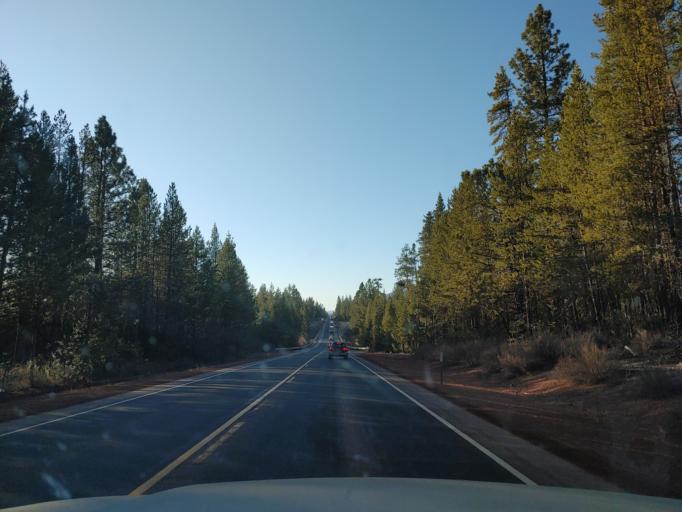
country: US
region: Oregon
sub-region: Deschutes County
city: La Pine
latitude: 43.3780
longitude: -121.7987
